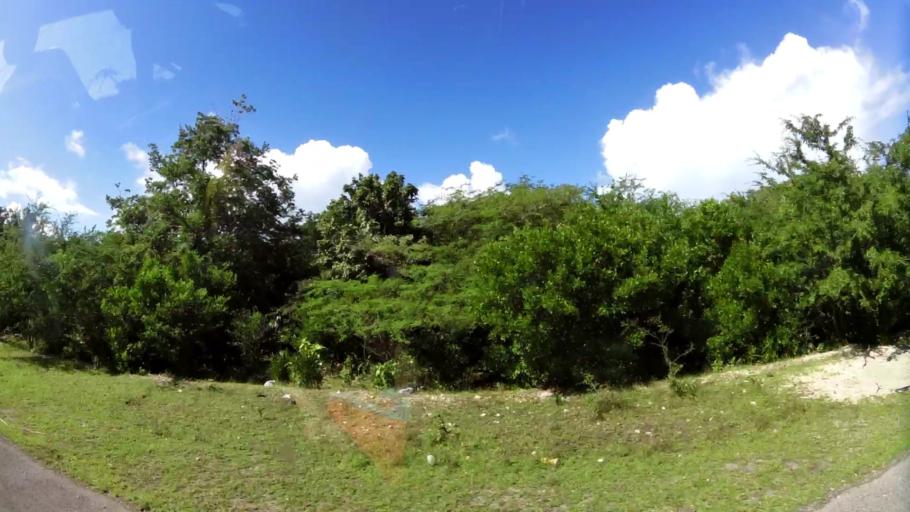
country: AG
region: Barbuda
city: Codrington
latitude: 17.6146
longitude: -61.8284
